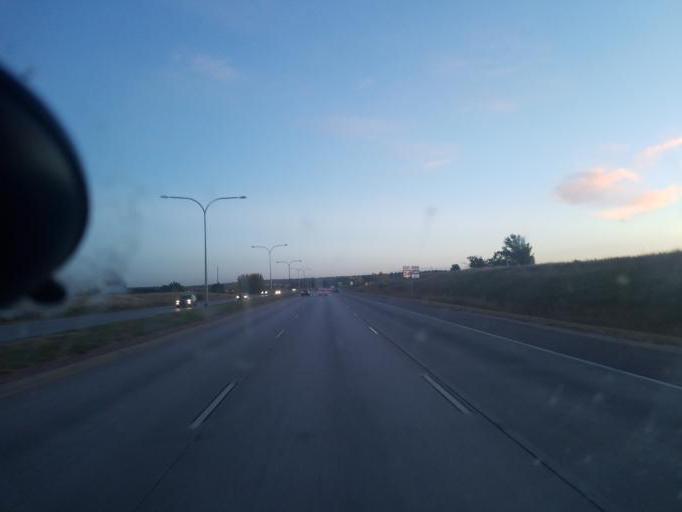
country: US
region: Colorado
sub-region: El Paso County
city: Cimarron Hills
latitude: 38.8260
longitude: -104.7237
